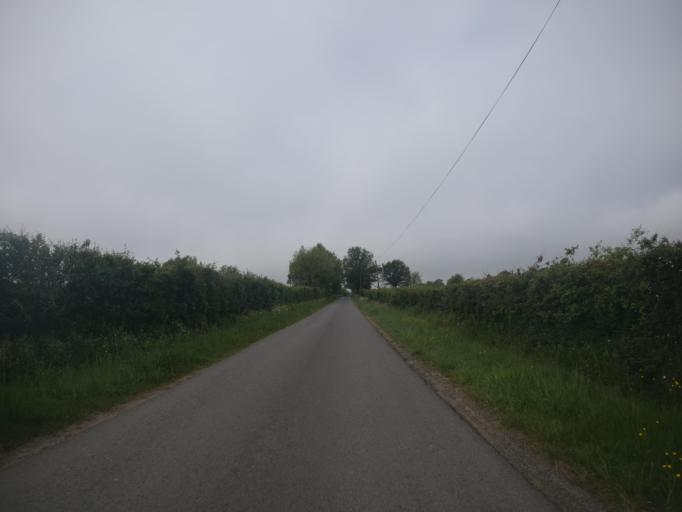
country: FR
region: Poitou-Charentes
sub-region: Departement des Deux-Sevres
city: Chiche
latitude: 46.8552
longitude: -0.3643
